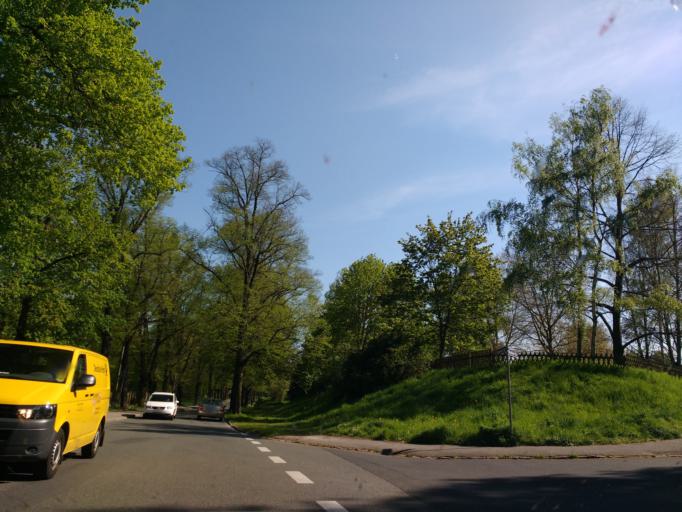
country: DE
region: Saxony-Anhalt
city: Zeitz
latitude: 51.0462
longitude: 12.1293
